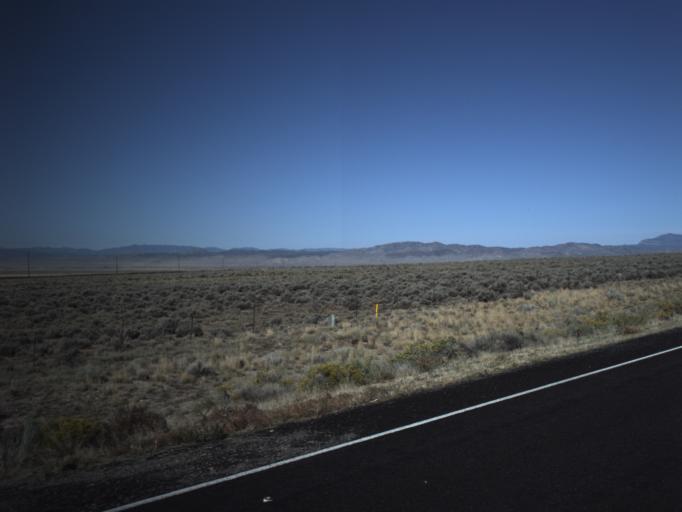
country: US
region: Utah
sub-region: Beaver County
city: Milford
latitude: 38.2347
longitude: -112.9347
